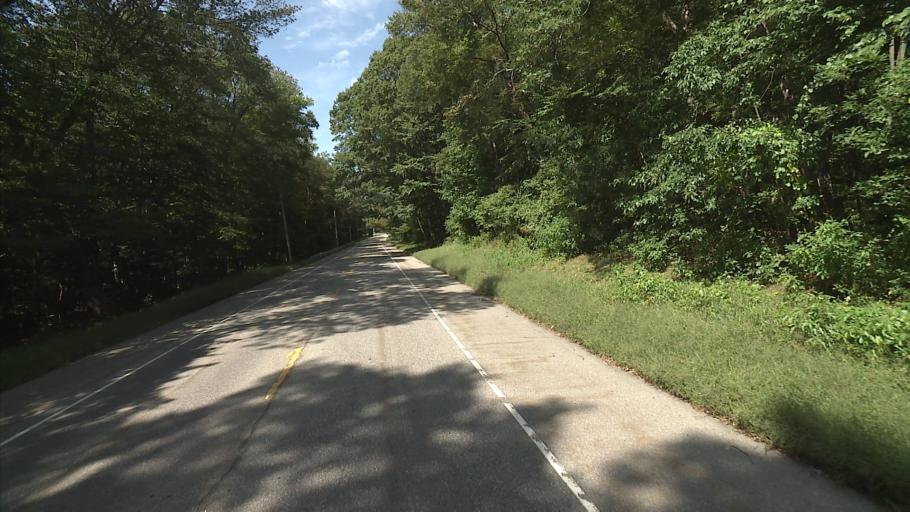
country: US
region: Connecticut
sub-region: New London County
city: Baltic
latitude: 41.5917
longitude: -72.1604
